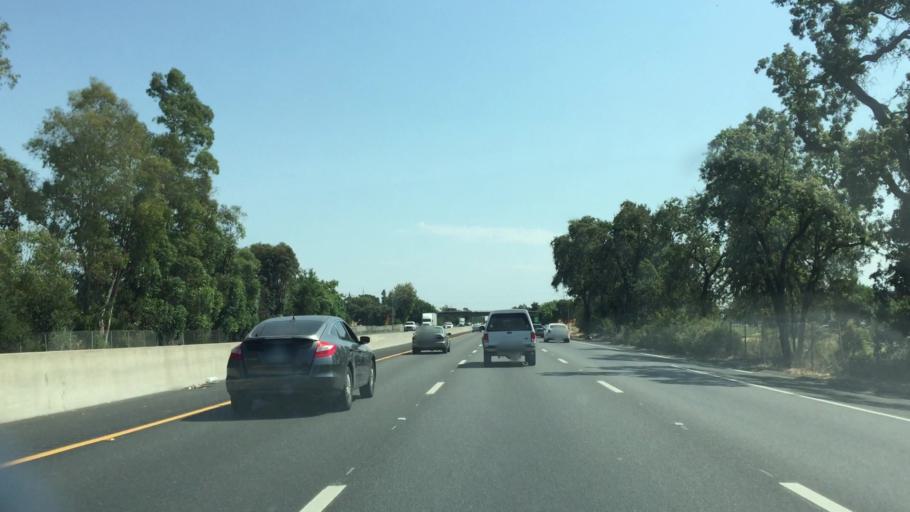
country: US
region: California
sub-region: San Joaquin County
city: Morada
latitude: 38.0412
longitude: -121.2586
